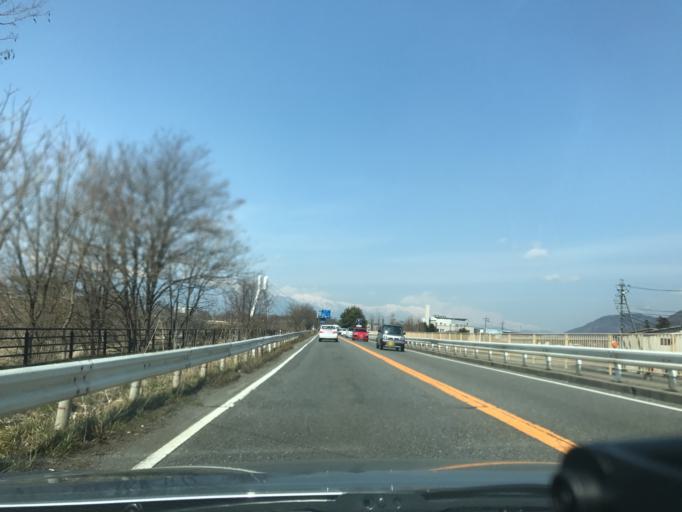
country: JP
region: Nagano
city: Matsumoto
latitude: 36.2620
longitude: 137.9474
